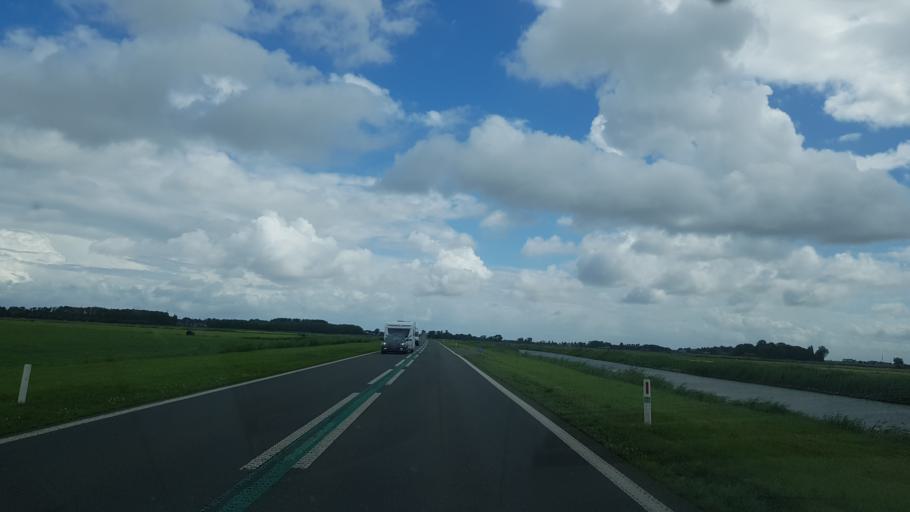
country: NL
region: Friesland
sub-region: Gemeente Dantumadiel
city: Walterswald
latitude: 53.3465
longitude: 6.0579
